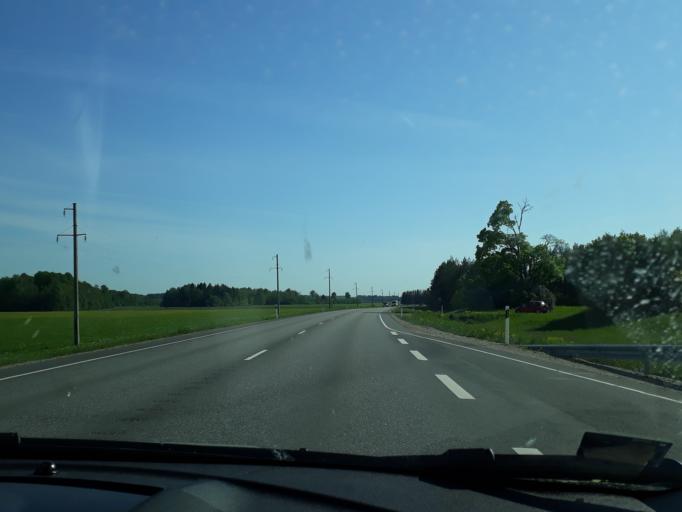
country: EE
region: Paernumaa
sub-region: Tootsi vald
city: Tootsi
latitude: 58.5636
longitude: 24.8713
